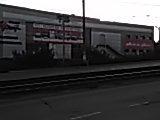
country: RU
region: Orenburg
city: Novotroitsk
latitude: 51.1994
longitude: 58.2999
